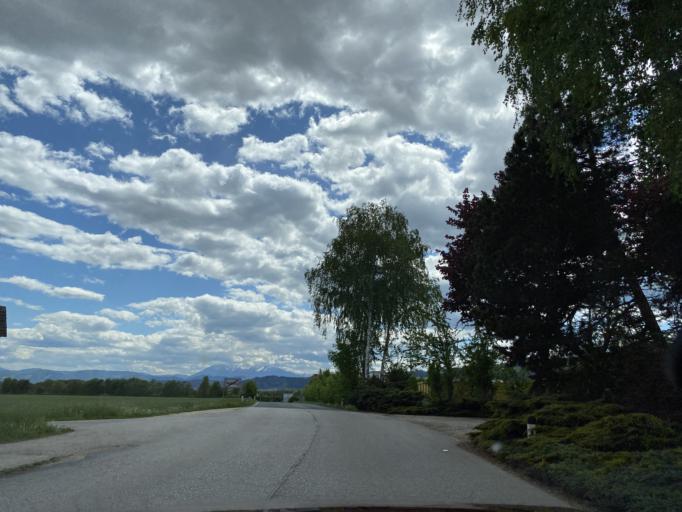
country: AT
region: Carinthia
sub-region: Politischer Bezirk Wolfsberg
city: Wolfsberg
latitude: 46.8265
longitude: 14.8273
